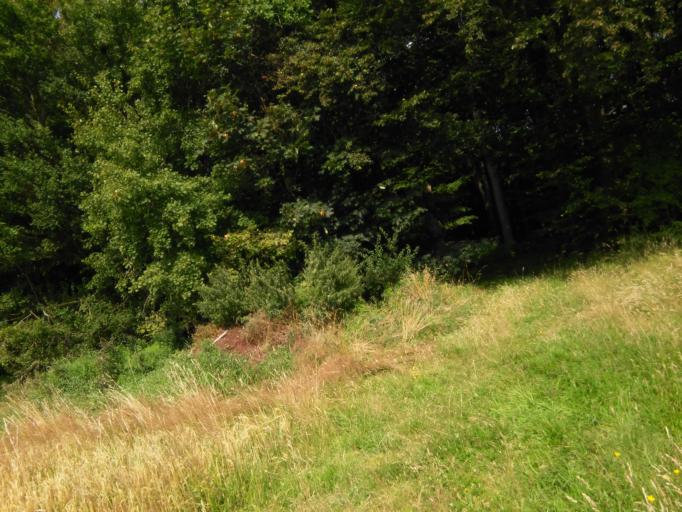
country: DK
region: Central Jutland
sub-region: Odder Kommune
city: Odder
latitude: 55.8812
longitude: 10.0412
